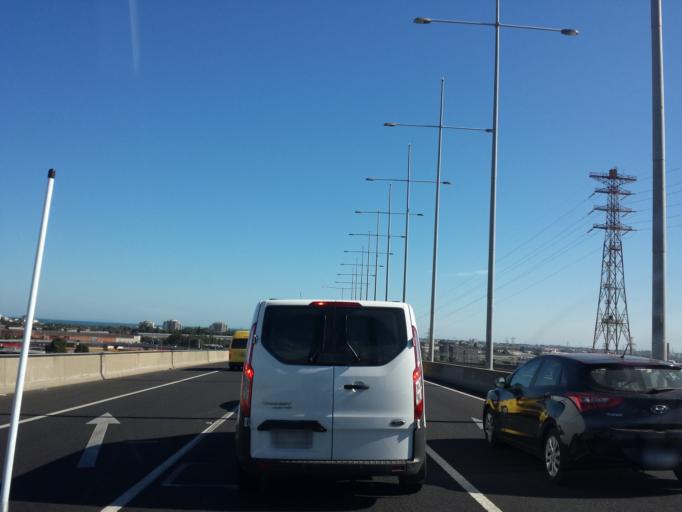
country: AU
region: Victoria
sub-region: Melbourne
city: Docklands
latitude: -37.8204
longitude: 144.9320
